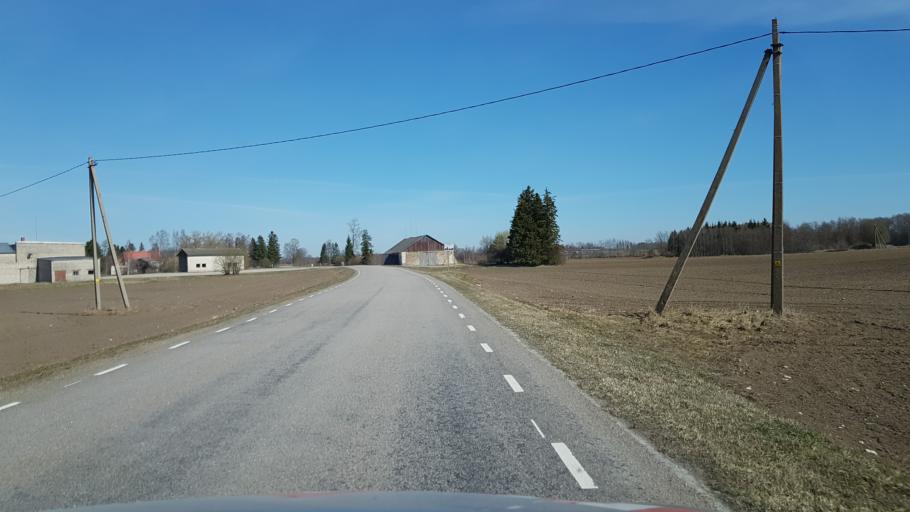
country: EE
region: Laeaene-Virumaa
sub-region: Vinni vald
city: Vinni
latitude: 59.2255
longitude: 26.3412
